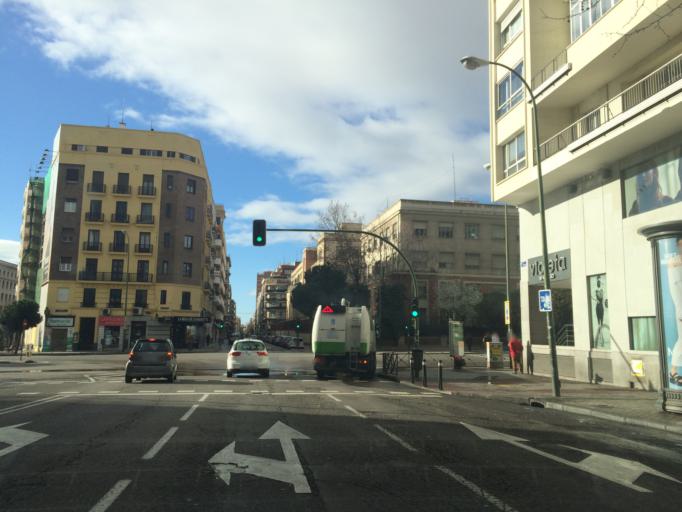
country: ES
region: Madrid
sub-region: Provincia de Madrid
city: Chamberi
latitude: 40.4470
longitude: -3.6955
